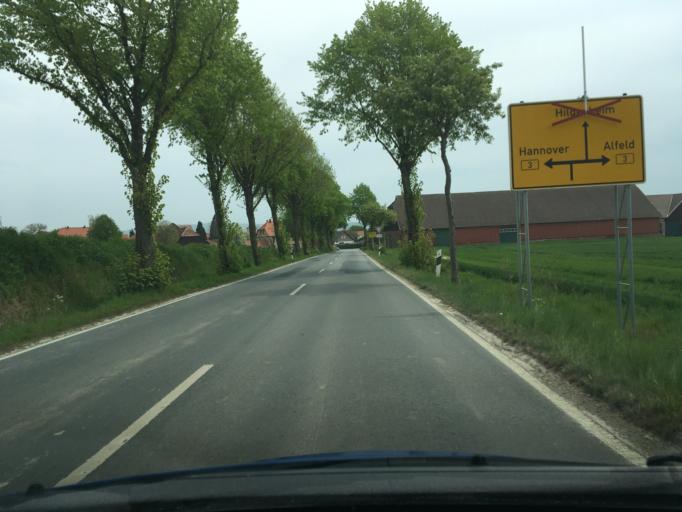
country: DE
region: Lower Saxony
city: Elze
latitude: 52.1537
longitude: 9.7366
